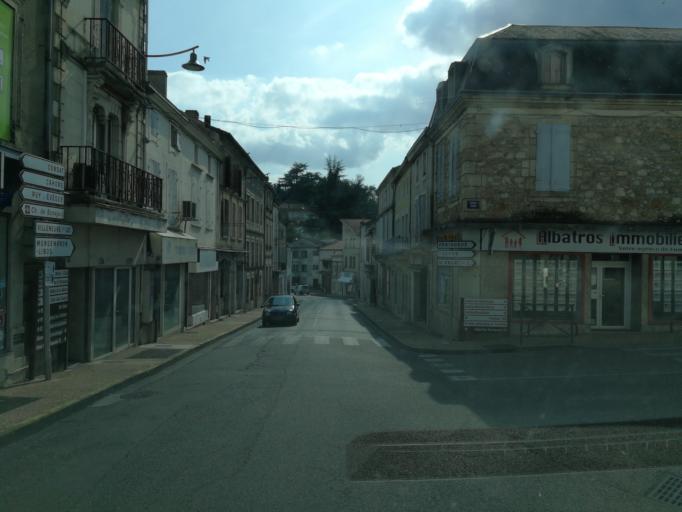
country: FR
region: Aquitaine
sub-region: Departement du Lot-et-Garonne
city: Fumel
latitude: 44.4978
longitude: 0.9678
